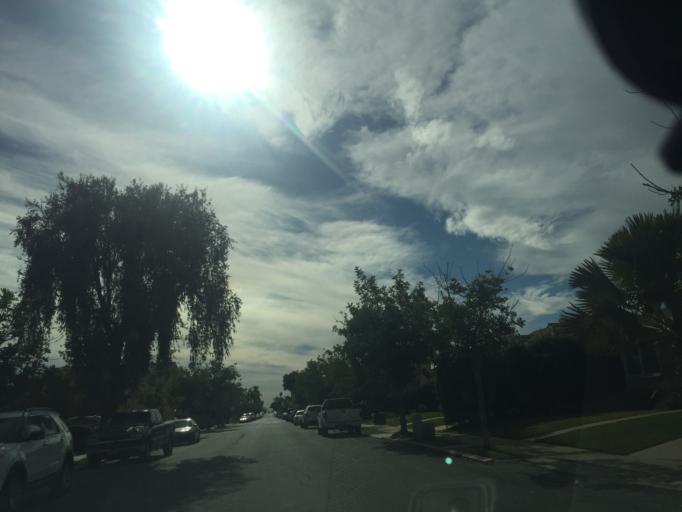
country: US
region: California
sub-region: San Diego County
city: Lemon Grove
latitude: 32.7620
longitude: -117.0857
